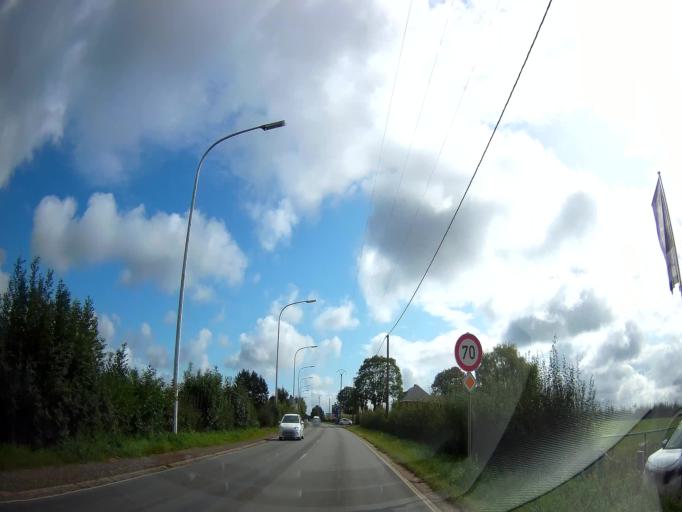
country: BE
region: Wallonia
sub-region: Province de Liege
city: Herve
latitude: 50.6371
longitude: 5.7680
